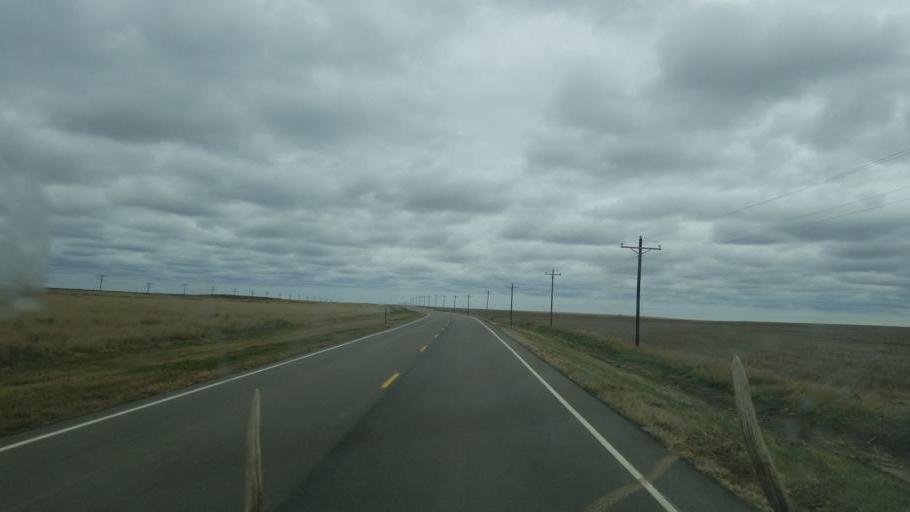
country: US
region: Colorado
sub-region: Kiowa County
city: Eads
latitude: 38.4929
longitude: -102.9295
